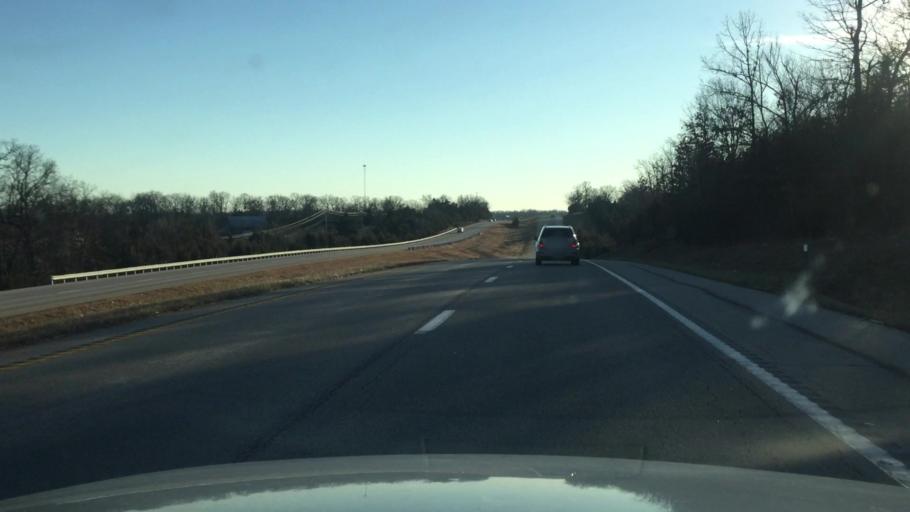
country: US
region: Missouri
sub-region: Cole County
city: Wardsville
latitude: 38.4592
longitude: -92.2971
